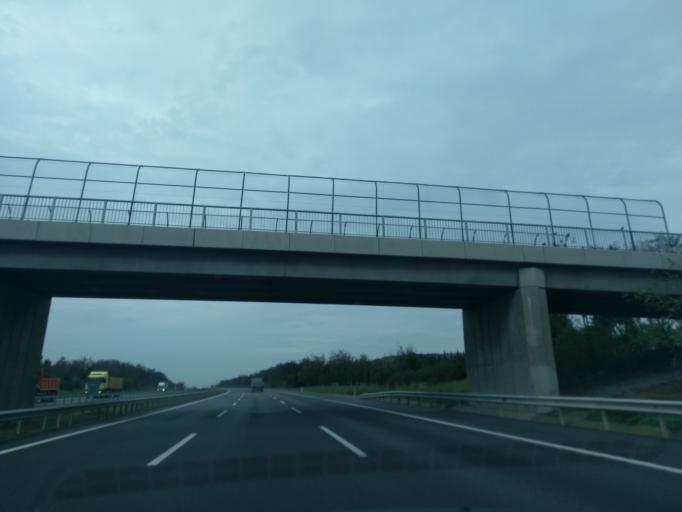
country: TR
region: Istanbul
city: Canta
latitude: 41.1602
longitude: 28.1368
